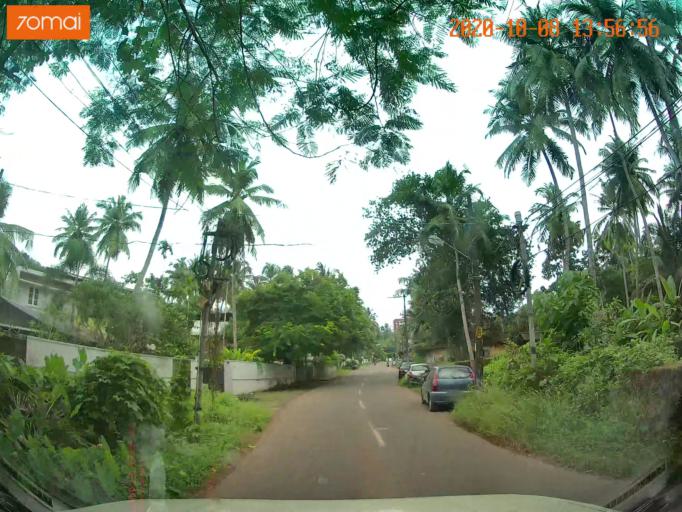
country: IN
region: Kerala
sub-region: Kozhikode
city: Kozhikode
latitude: 11.2910
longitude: 75.8009
